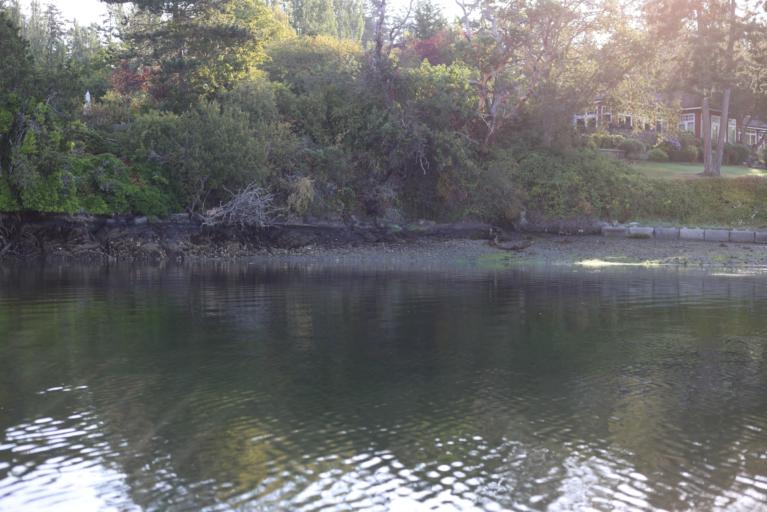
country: CA
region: British Columbia
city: North Saanich
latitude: 48.6765
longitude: -123.4128
